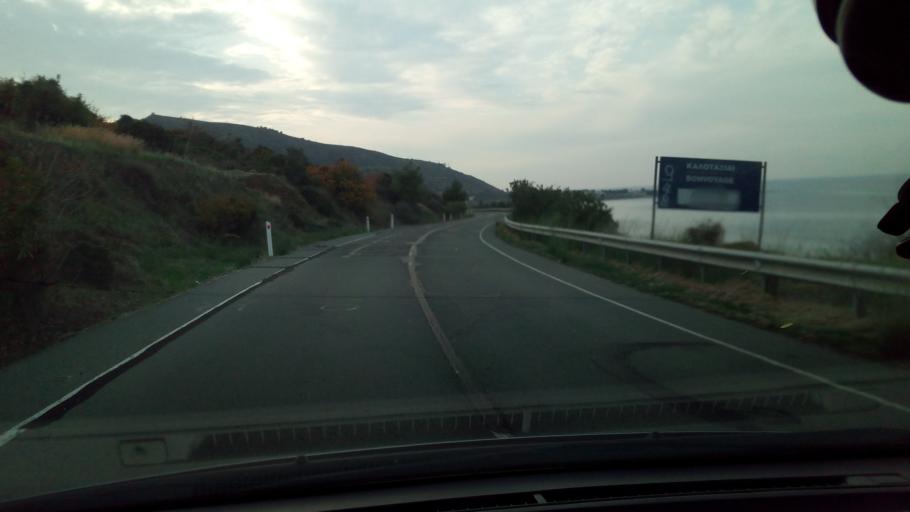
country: CY
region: Lefkosia
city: Kato Pyrgos
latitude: 35.1693
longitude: 32.5713
